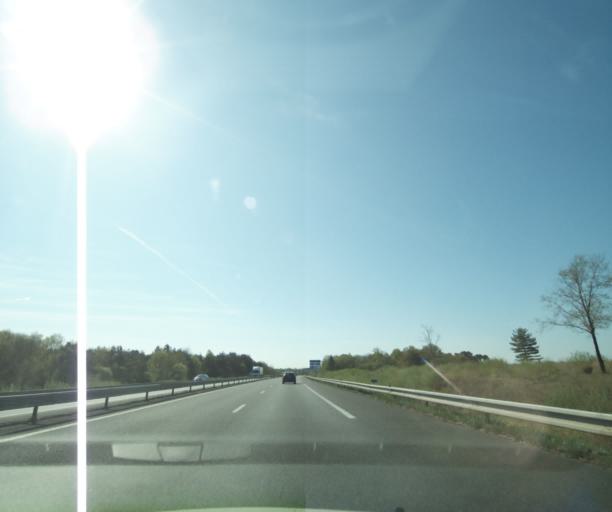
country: FR
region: Centre
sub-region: Departement du Loir-et-Cher
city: Lamotte-Beuvron
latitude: 47.5660
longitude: 2.0060
